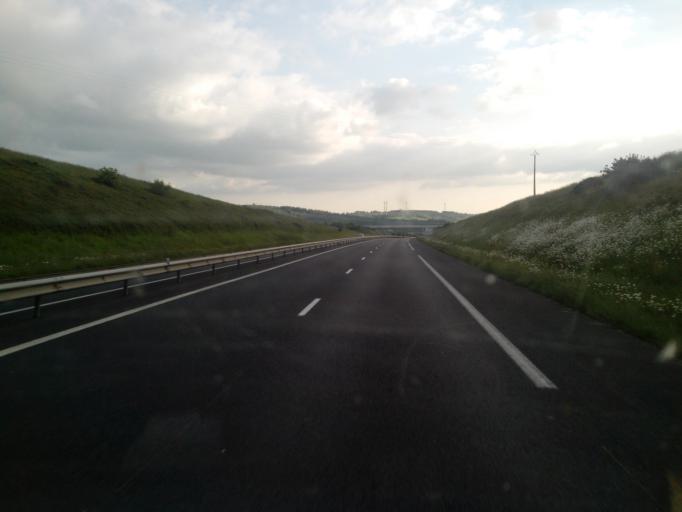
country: FR
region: Lower Normandy
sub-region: Departement de la Manche
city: Saint-Amand
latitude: 48.9936
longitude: -0.9198
